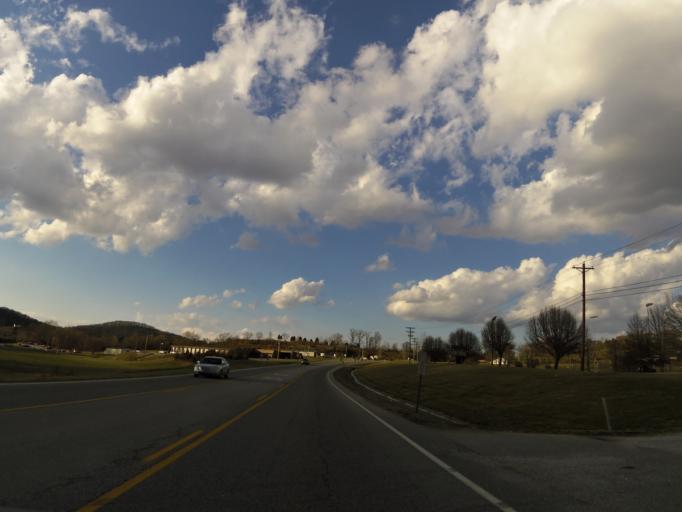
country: US
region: Tennessee
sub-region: Smith County
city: South Carthage
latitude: 36.2229
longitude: -85.9487
